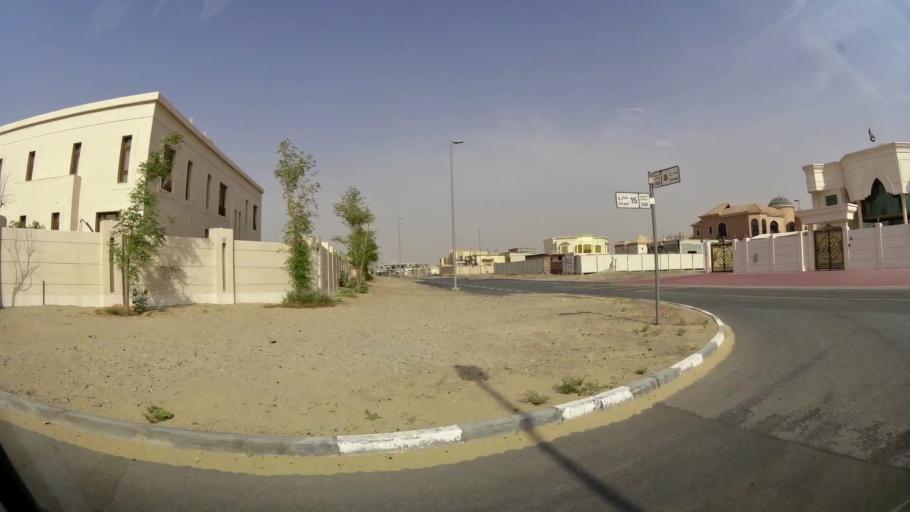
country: AE
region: Ash Shariqah
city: Sharjah
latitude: 25.2595
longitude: 55.4623
